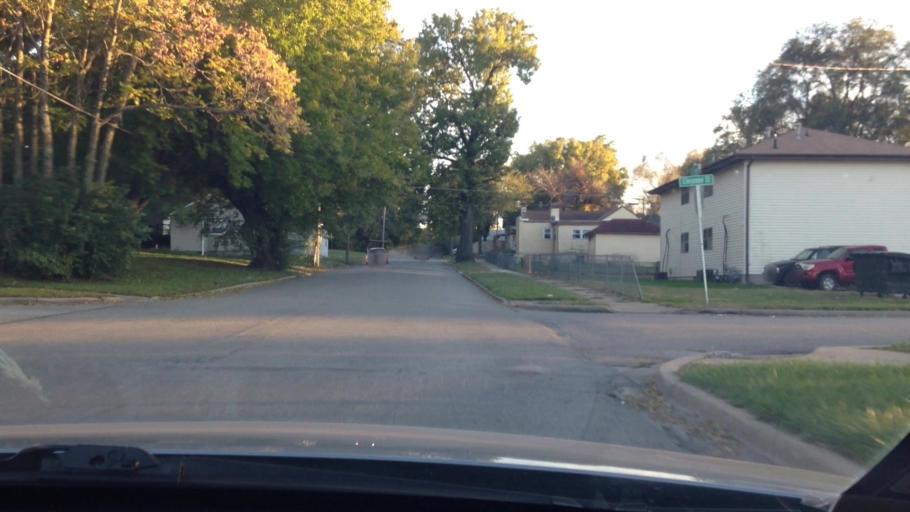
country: US
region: Kansas
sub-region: Leavenworth County
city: Leavenworth
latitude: 39.3276
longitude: -94.9190
